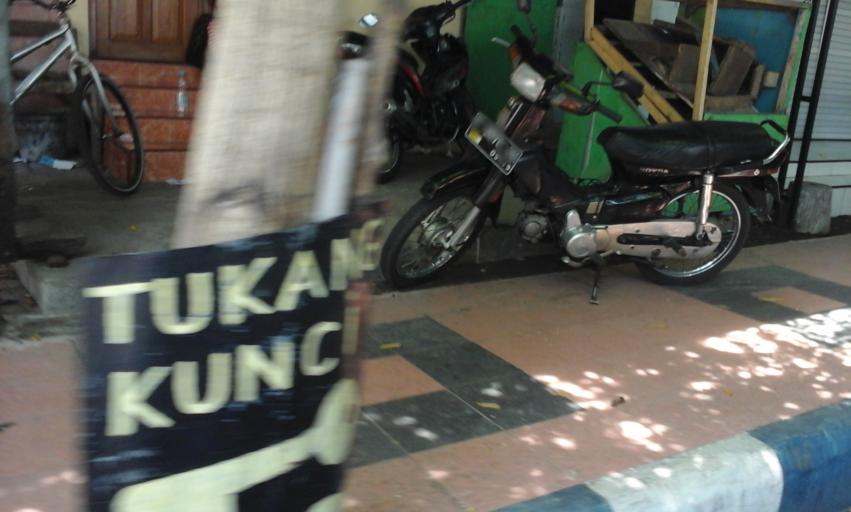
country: ID
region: East Java
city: Cungking
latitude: -8.2153
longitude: 114.3555
